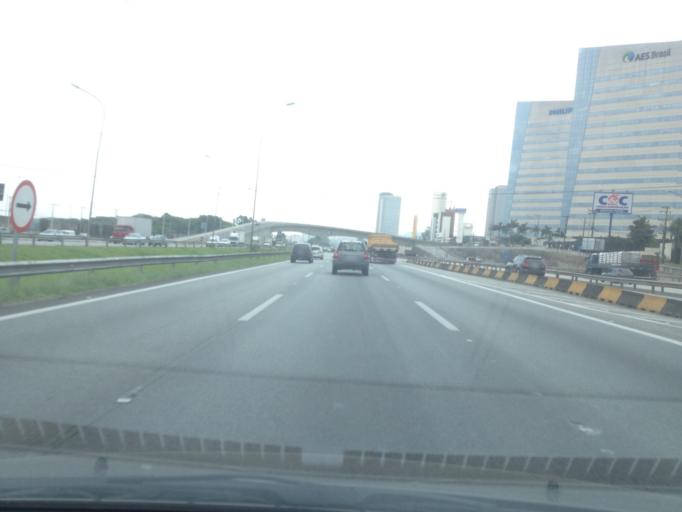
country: BR
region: Sao Paulo
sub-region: Carapicuiba
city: Carapicuiba
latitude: -23.5070
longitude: -46.8349
